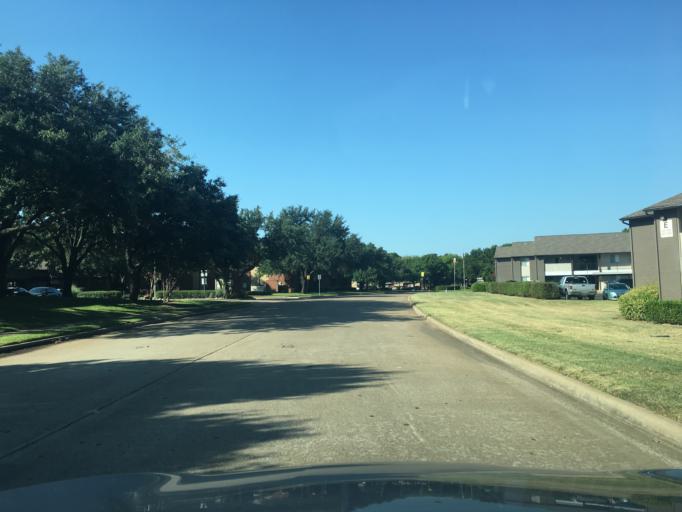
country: US
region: Texas
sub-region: Dallas County
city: Addison
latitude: 32.9626
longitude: -96.8497
